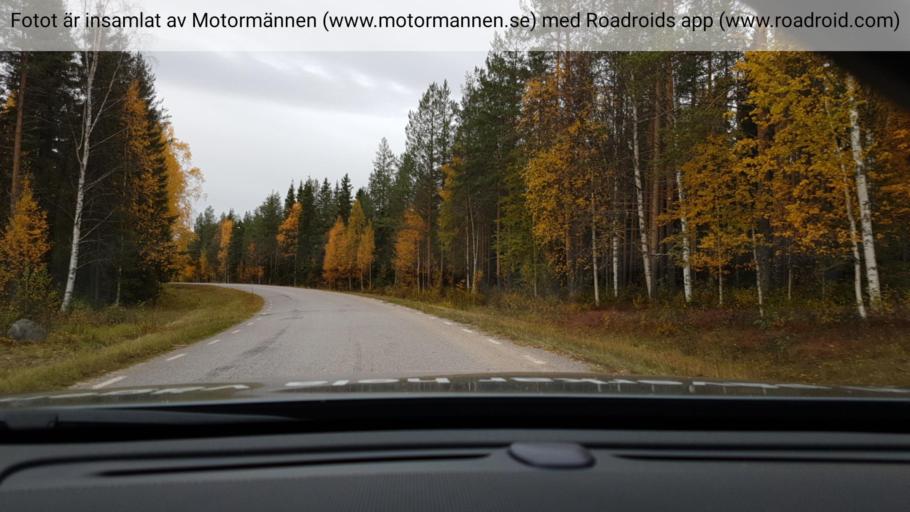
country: SE
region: Norrbotten
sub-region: Overkalix Kommun
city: OEverkalix
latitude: 66.2381
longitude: 22.9722
